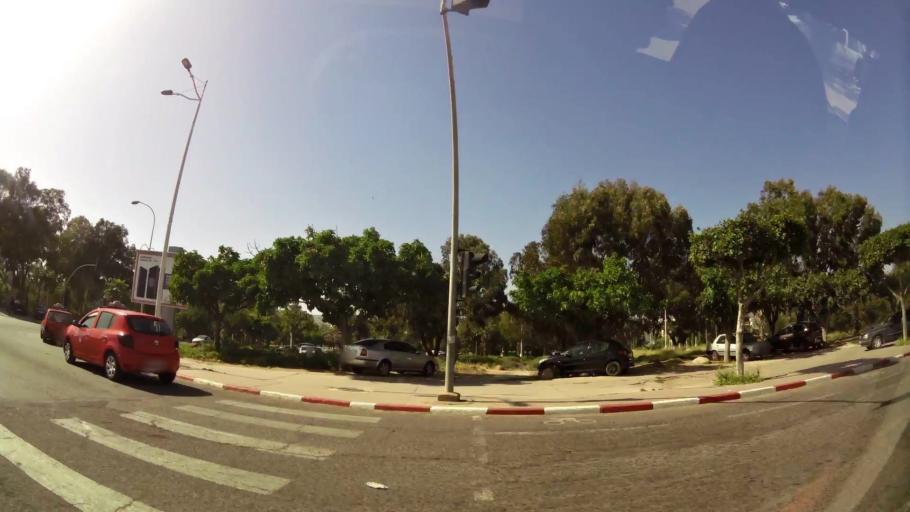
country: MA
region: Souss-Massa-Draa
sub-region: Agadir-Ida-ou-Tnan
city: Agadir
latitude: 30.4189
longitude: -9.5907
